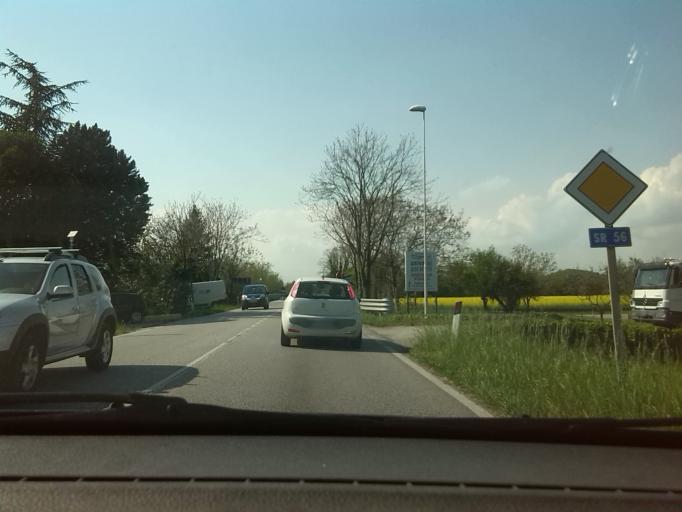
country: IT
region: Friuli Venezia Giulia
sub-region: Provincia di Udine
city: San Giovanni al Natisone
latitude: 45.9760
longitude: 13.3921
